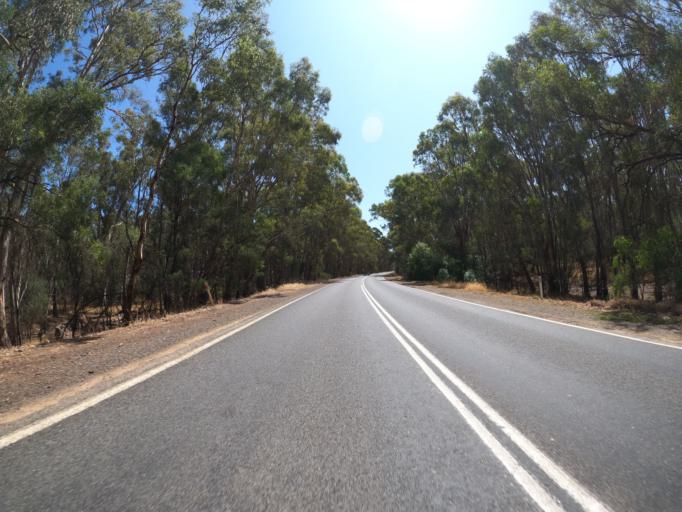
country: AU
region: New South Wales
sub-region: Corowa Shire
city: Corowa
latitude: -36.0692
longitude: 146.1974
